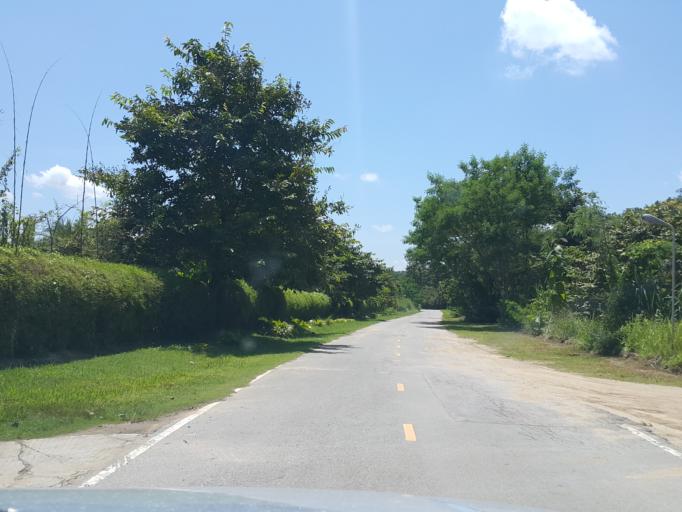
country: TH
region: Chiang Mai
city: San Kamphaeng
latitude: 18.6873
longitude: 99.1725
